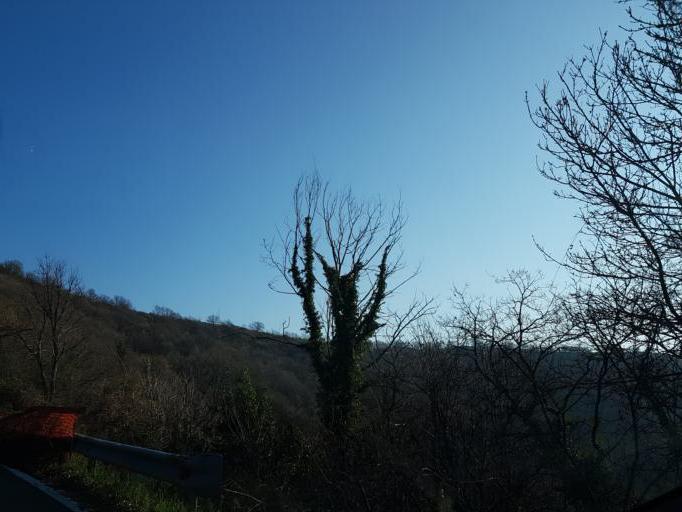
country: IT
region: Liguria
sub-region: Provincia di Genova
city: Piccarello
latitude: 44.4618
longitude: 8.9544
